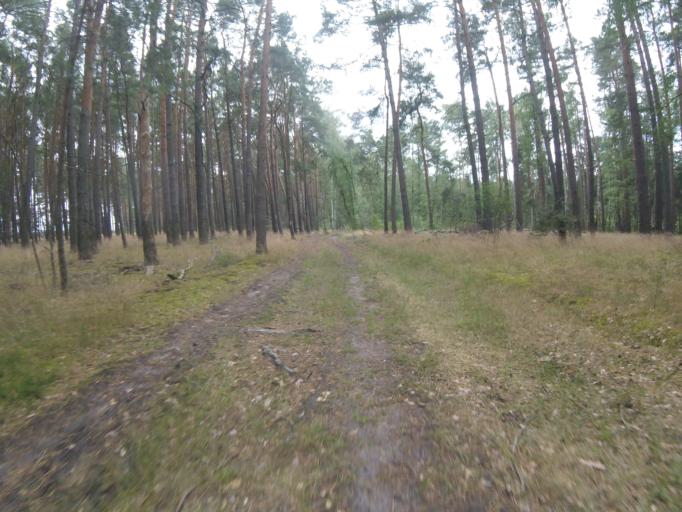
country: DE
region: Brandenburg
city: Bestensee
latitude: 52.2708
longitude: 13.7143
